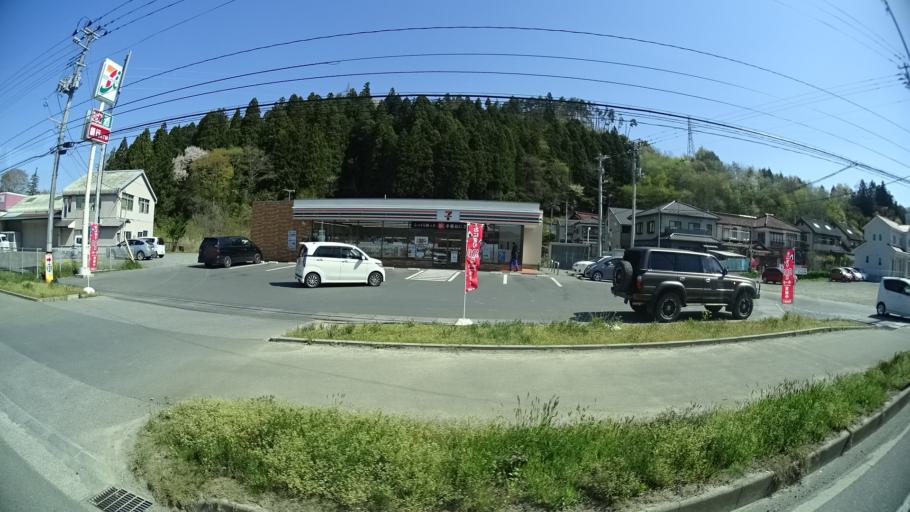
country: JP
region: Iwate
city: Ofunato
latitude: 38.9208
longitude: 141.5877
